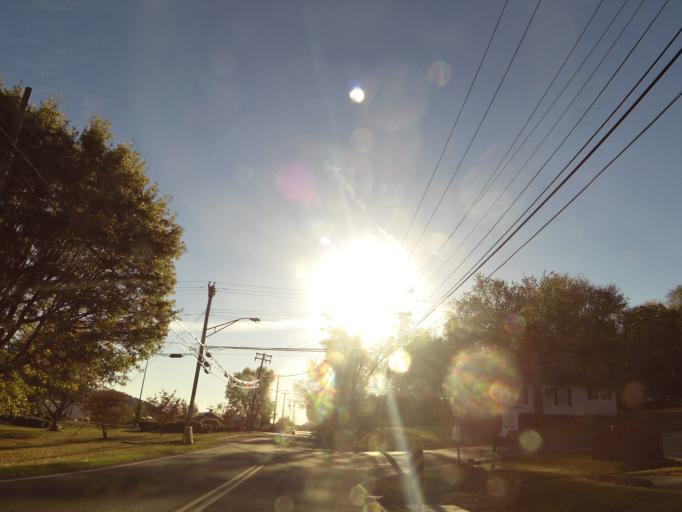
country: US
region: Tennessee
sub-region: Knox County
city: Knoxville
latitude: 36.0104
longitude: -83.9434
